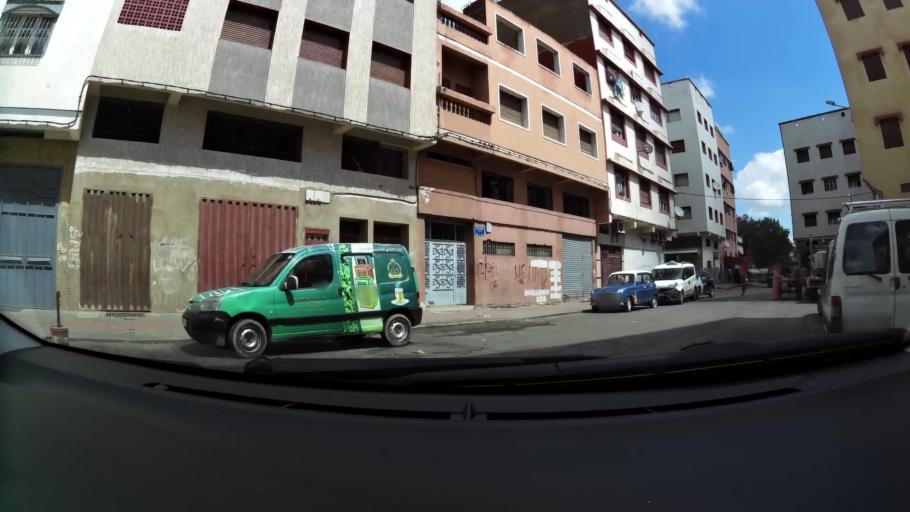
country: MA
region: Grand Casablanca
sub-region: Casablanca
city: Casablanca
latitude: 33.5395
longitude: -7.5682
